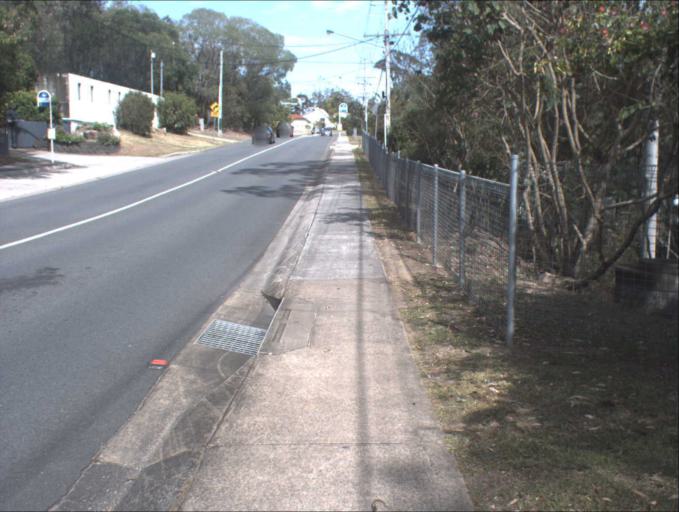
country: AU
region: Queensland
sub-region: Logan
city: Slacks Creek
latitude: -27.6279
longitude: 153.1496
